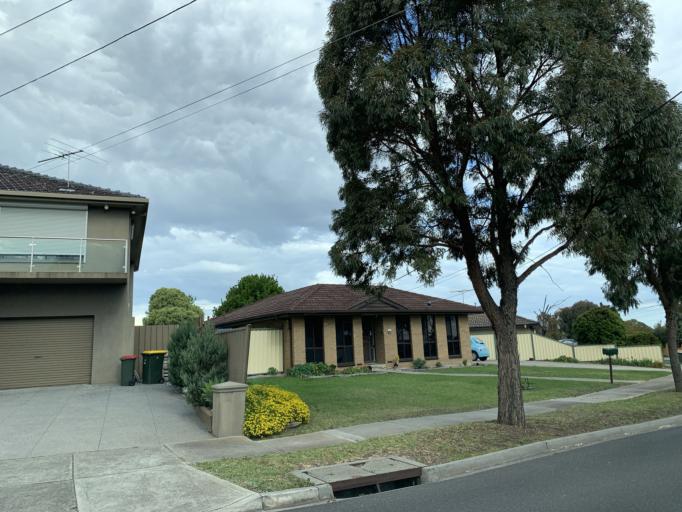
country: AU
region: Victoria
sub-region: Moonee Valley
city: Keilor East
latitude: -37.7469
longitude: 144.8490
